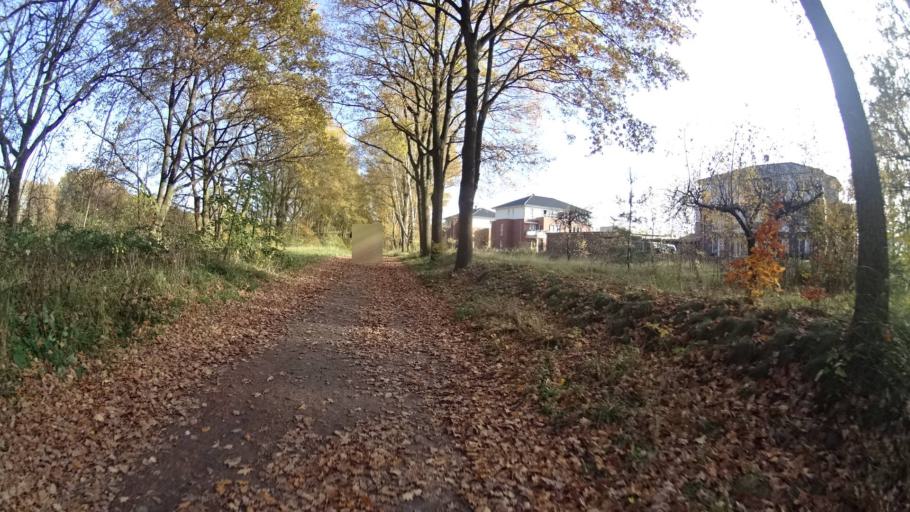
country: DE
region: Lower Saxony
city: Lueneburg
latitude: 53.2566
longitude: 10.4339
